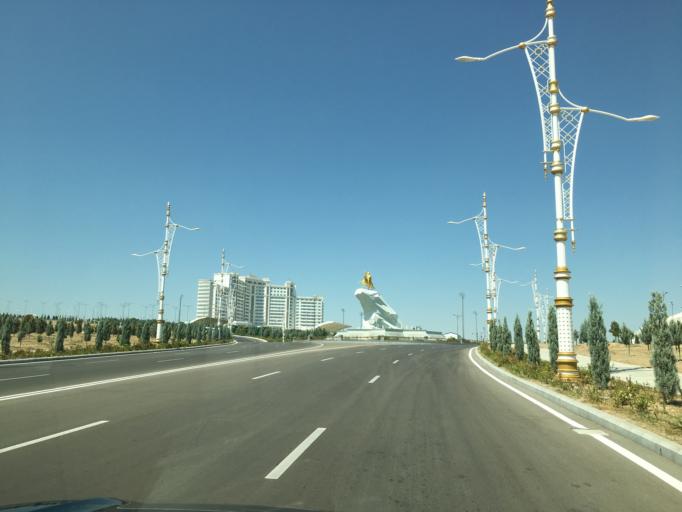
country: TM
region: Ahal
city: Ashgabat
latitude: 37.9240
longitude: 58.3498
